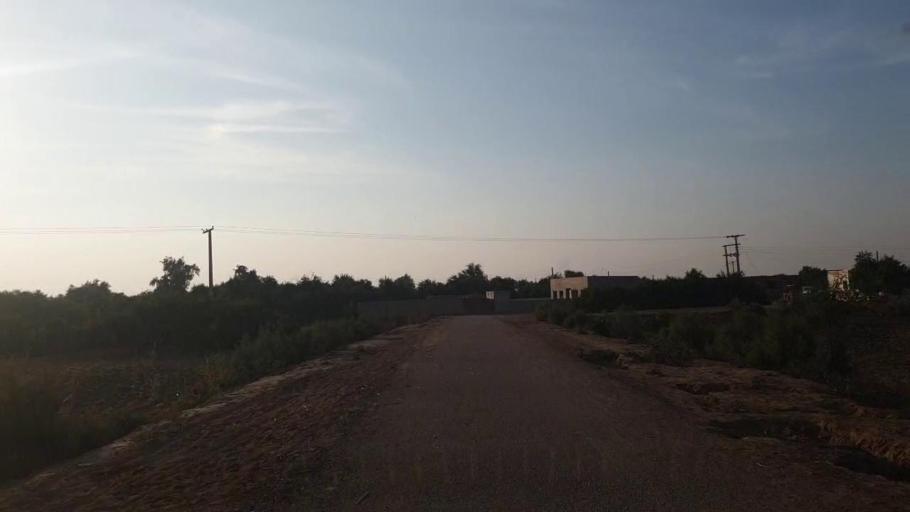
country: PK
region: Sindh
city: Sann
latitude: 25.9263
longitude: 68.1747
